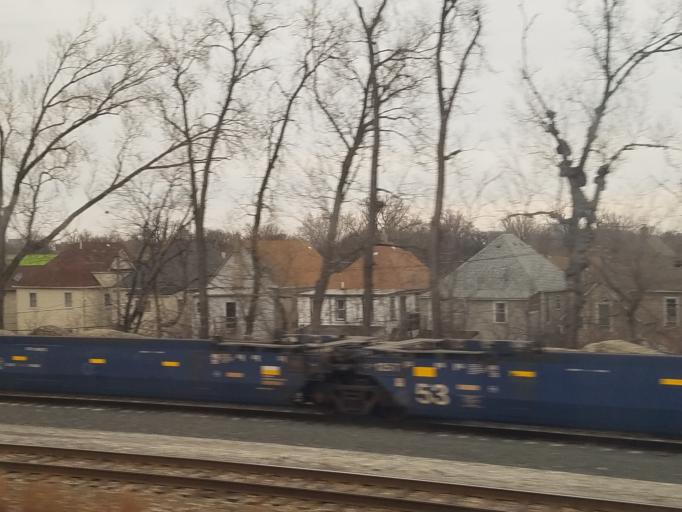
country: US
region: Illinois
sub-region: Cook County
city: Chicago
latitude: 41.7661
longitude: -87.6040
